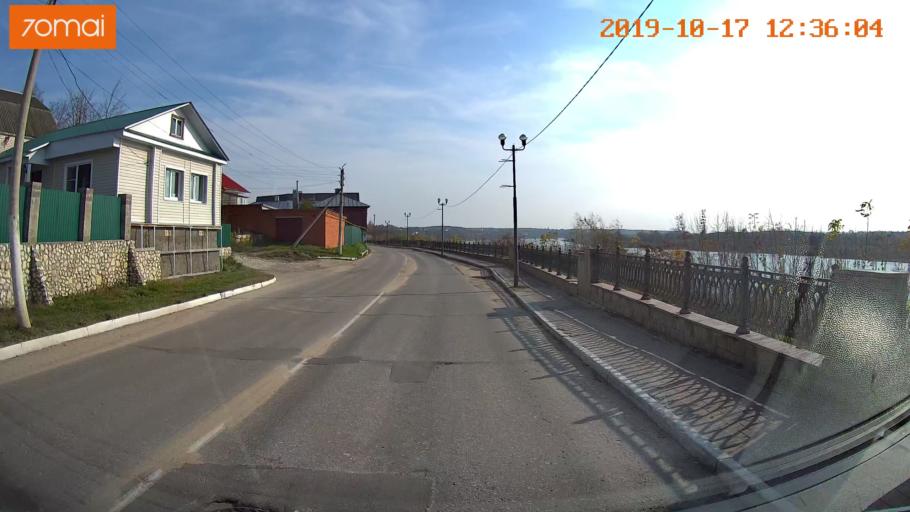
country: RU
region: Rjazan
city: Kasimov
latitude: 54.9408
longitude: 41.3727
